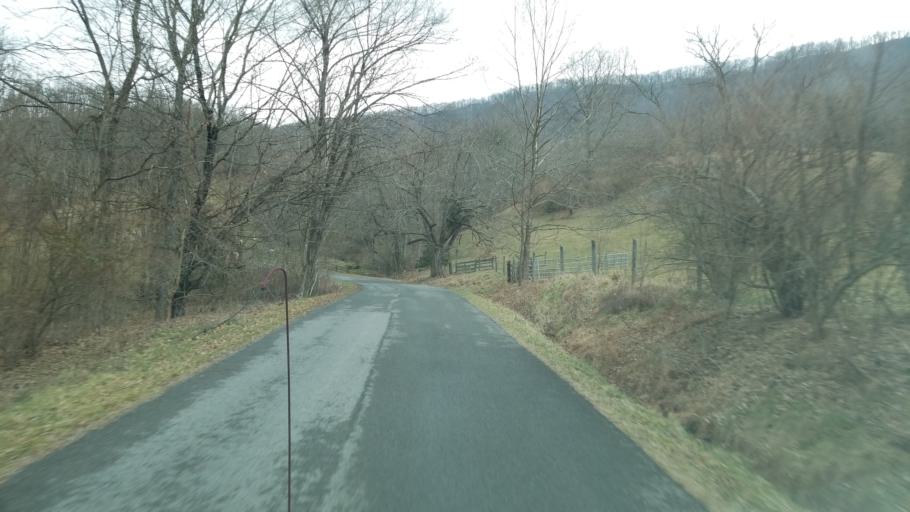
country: US
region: Virginia
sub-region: Giles County
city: Pearisburg
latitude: 37.2183
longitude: -80.7034
